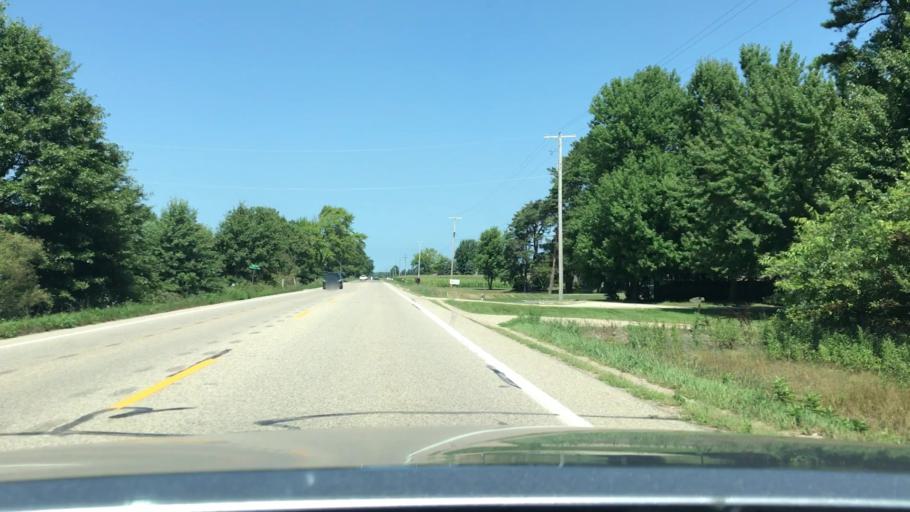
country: US
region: Michigan
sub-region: Ottawa County
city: Allendale
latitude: 42.9484
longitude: -86.0822
